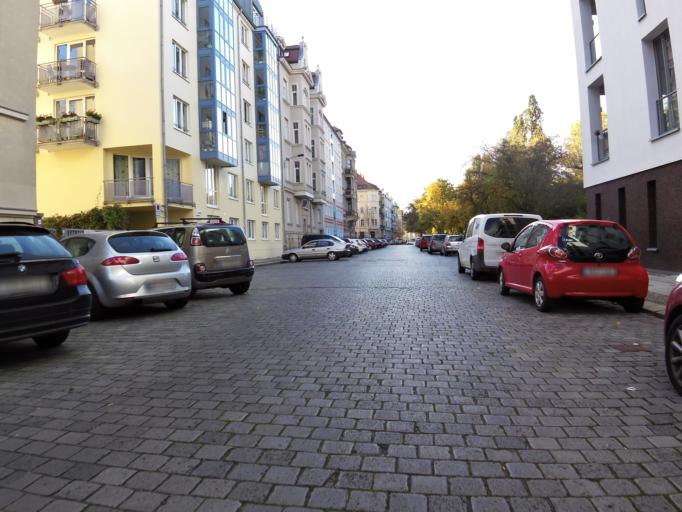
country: DE
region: Saxony
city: Leipzig
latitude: 51.3186
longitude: 12.3755
